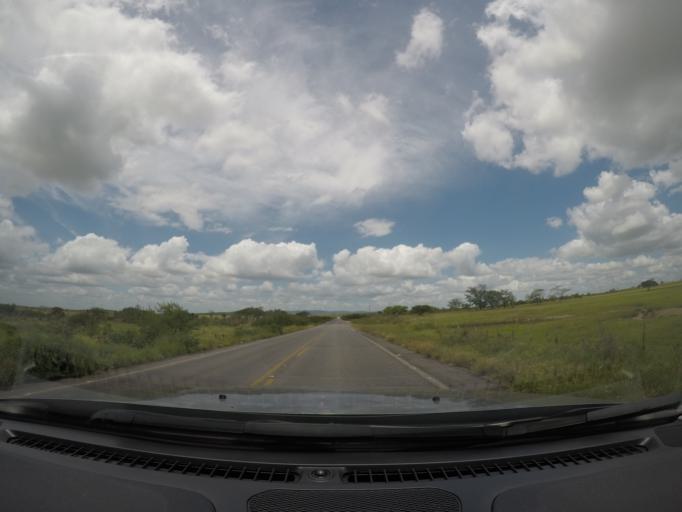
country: BR
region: Bahia
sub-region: Ipira
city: Ipira
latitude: -12.2471
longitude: -39.8089
